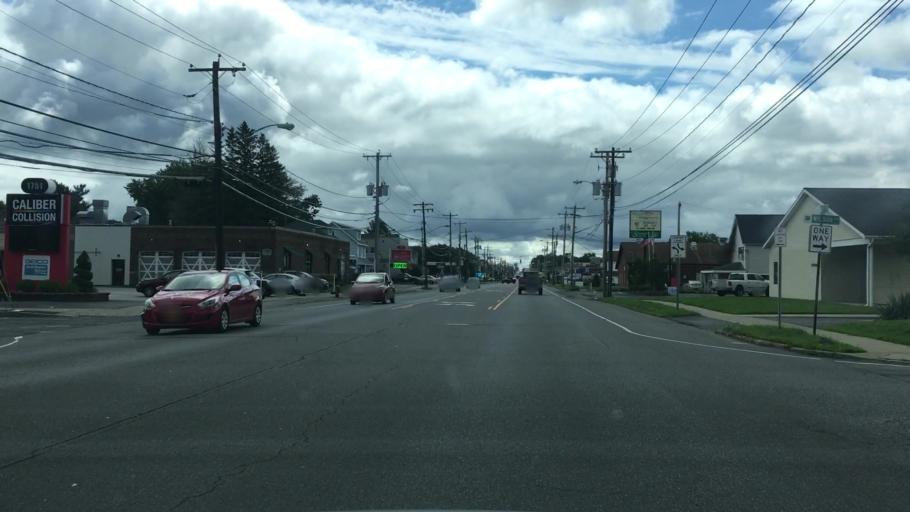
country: US
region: New York
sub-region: Schenectady County
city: Schenectady
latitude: 42.7826
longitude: -73.9065
